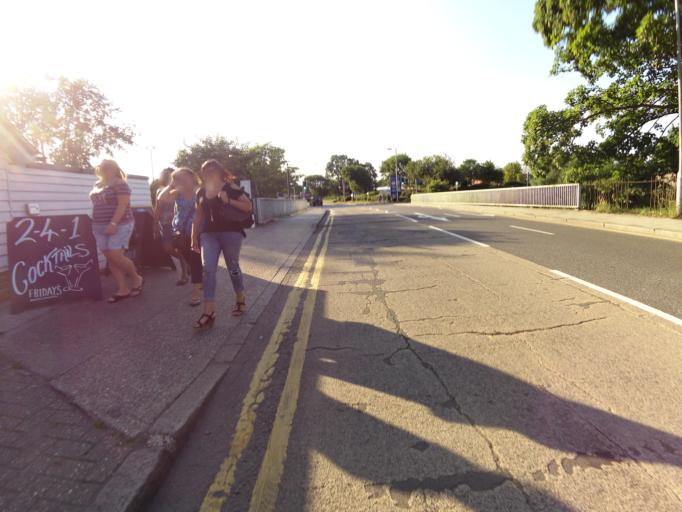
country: GB
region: England
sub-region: Essex
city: Chelmsford
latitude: 51.7361
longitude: 0.4794
